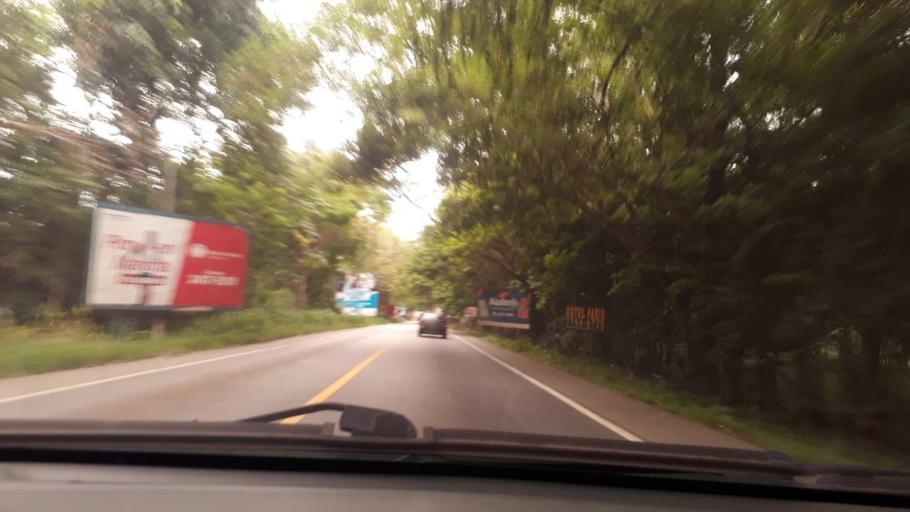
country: GT
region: Izabal
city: Morales
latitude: 15.5028
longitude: -88.8453
